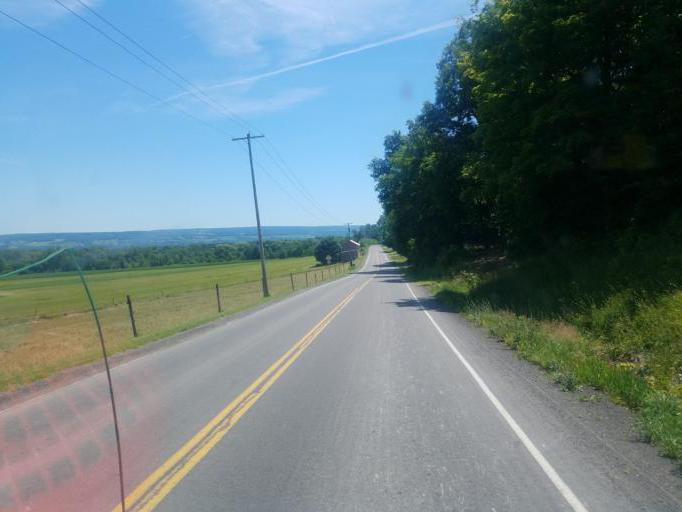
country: US
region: New York
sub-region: Yates County
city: Dundee
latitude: 42.5978
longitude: -76.9642
